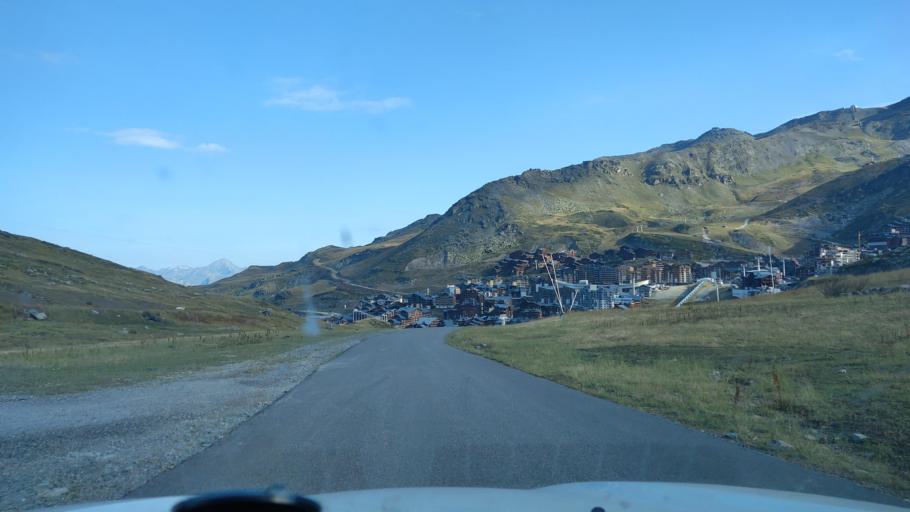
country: FR
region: Rhone-Alpes
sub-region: Departement de la Savoie
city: Val Thorens
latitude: 45.2902
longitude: 6.5829
